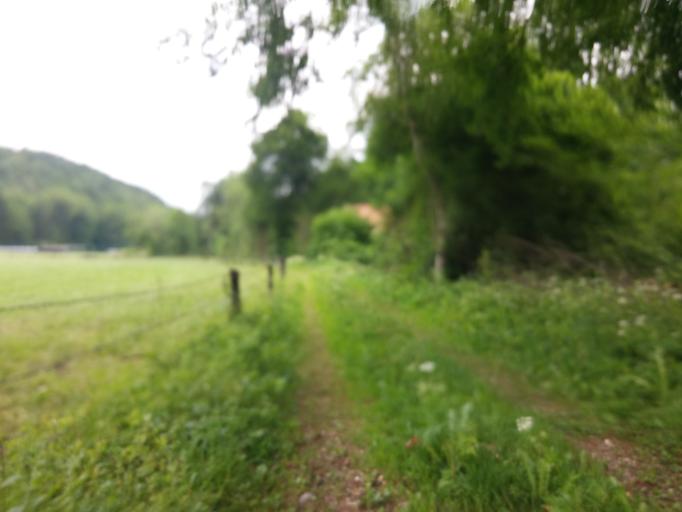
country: DE
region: Bavaria
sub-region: Swabia
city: Lautrach
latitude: 47.8908
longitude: 10.1083
